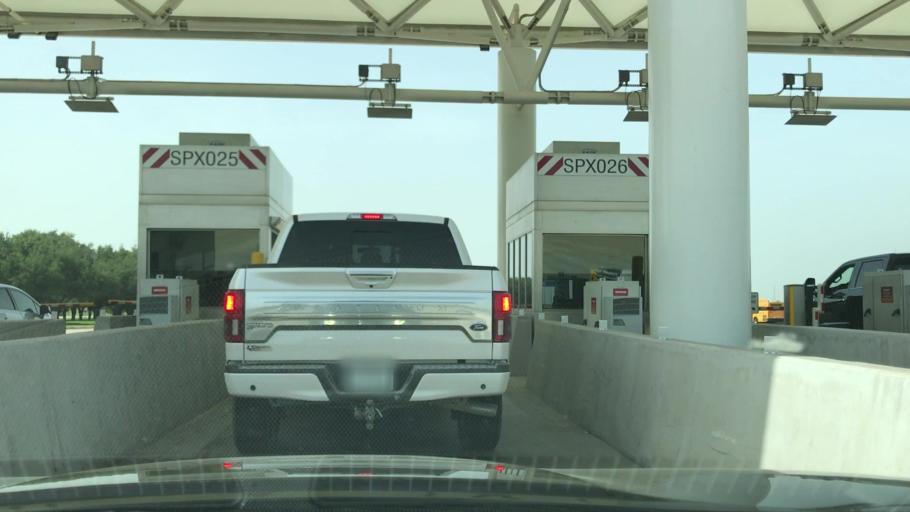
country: US
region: Texas
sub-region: Tarrant County
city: Euless
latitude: 32.8659
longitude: -97.0412
